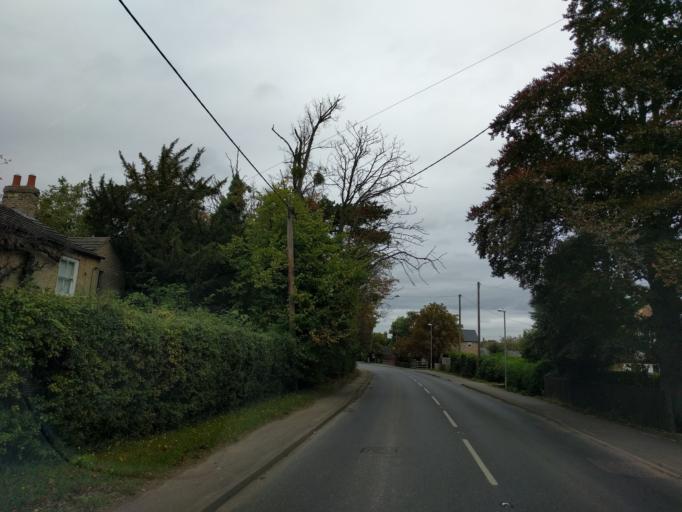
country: GB
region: England
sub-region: Cambridgeshire
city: Earith
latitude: 52.3062
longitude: 0.0526
